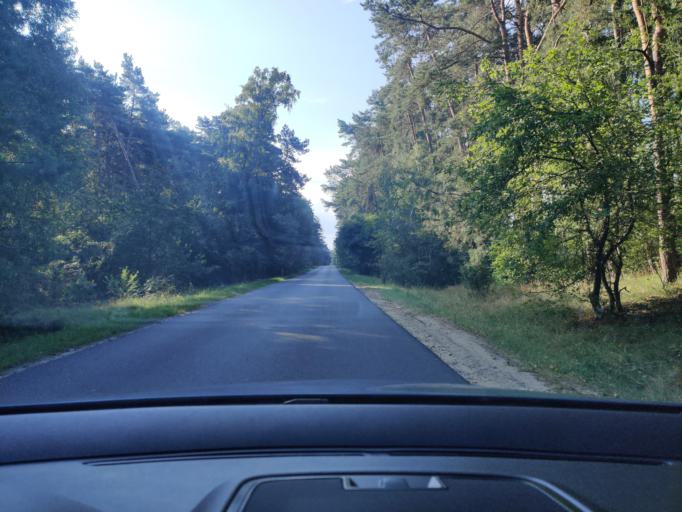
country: PL
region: Greater Poland Voivodeship
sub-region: Konin
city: Konin
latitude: 52.1827
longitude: 18.3324
